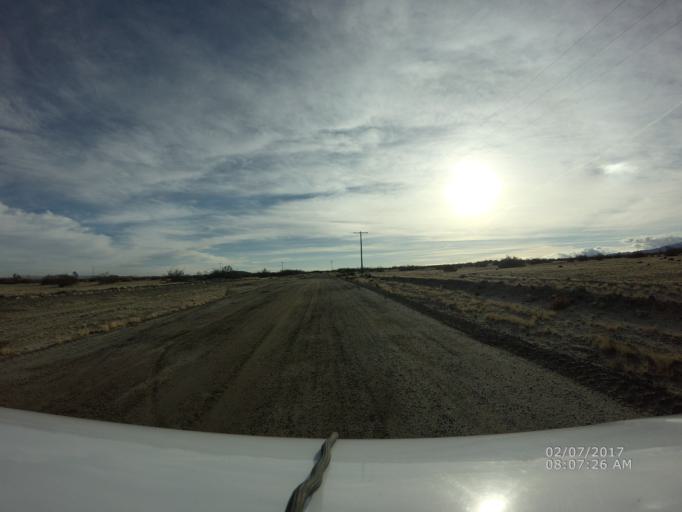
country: US
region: California
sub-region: Los Angeles County
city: Lake Los Angeles
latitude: 34.5724
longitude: -117.7226
